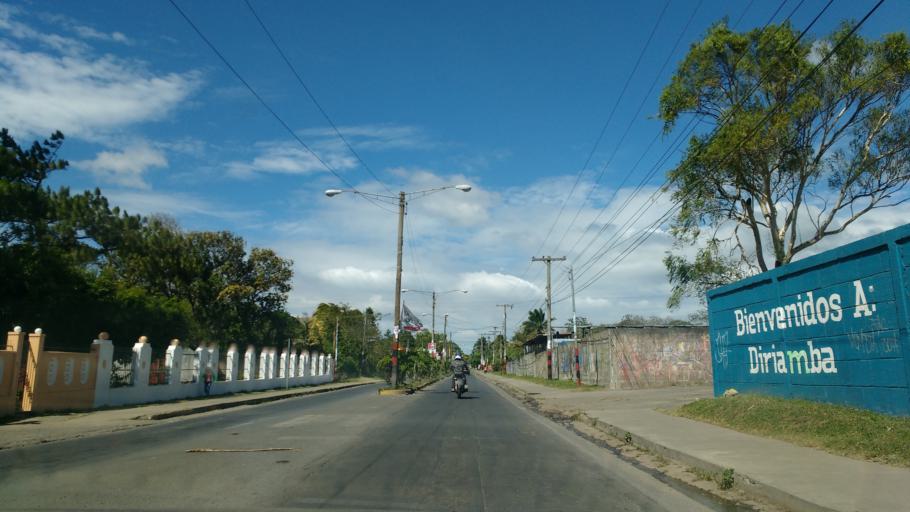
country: NI
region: Carazo
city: Diriamba
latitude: 11.8644
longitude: -86.2394
